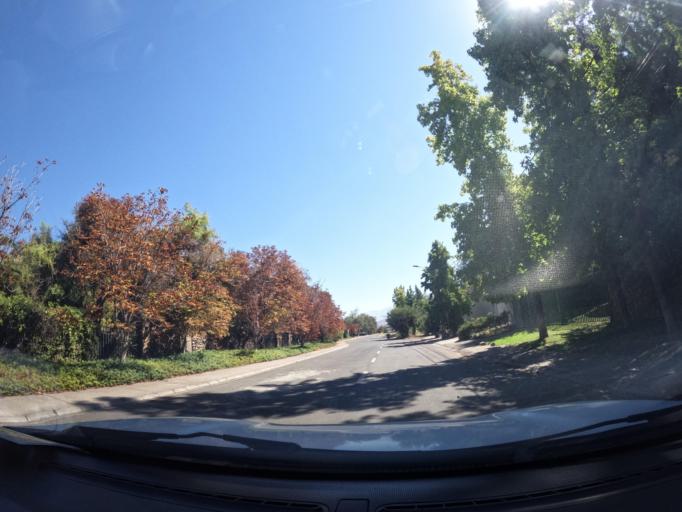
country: CL
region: Santiago Metropolitan
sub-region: Provincia de Santiago
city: Villa Presidente Frei, Nunoa, Santiago, Chile
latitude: -33.4756
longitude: -70.5239
